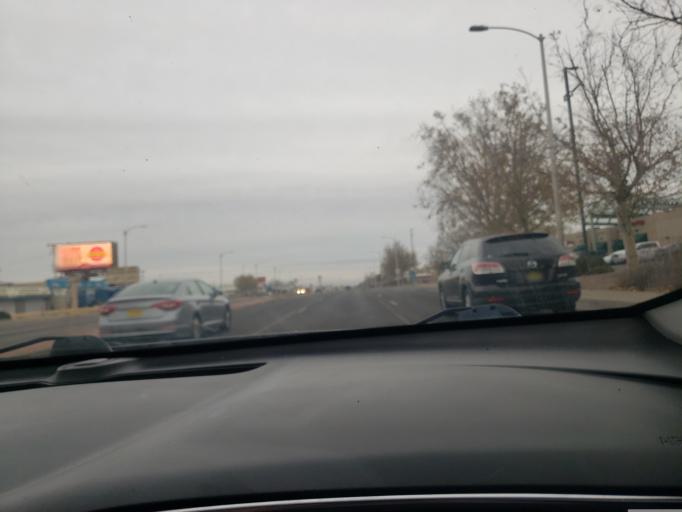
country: US
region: New Mexico
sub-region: Bernalillo County
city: Albuquerque
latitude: 35.0861
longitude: -106.5865
